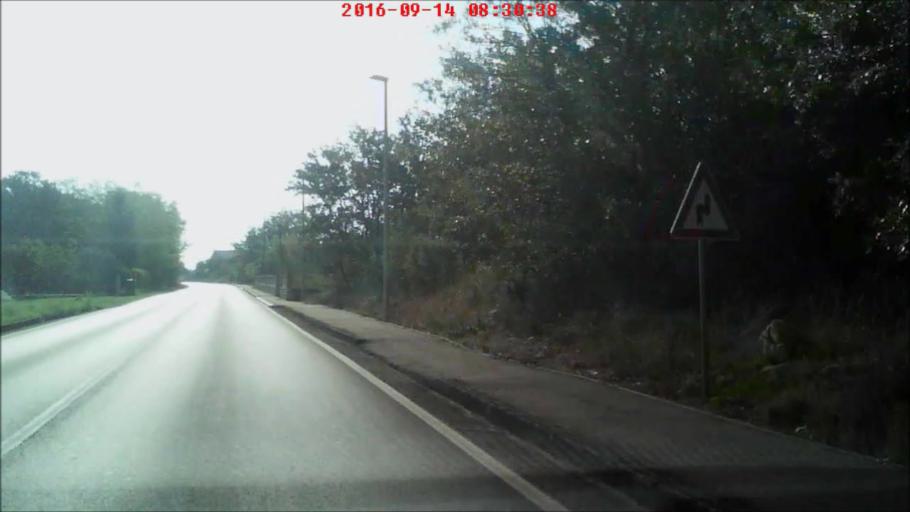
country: HR
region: Zadarska
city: Zadar
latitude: 44.1714
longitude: 15.2906
